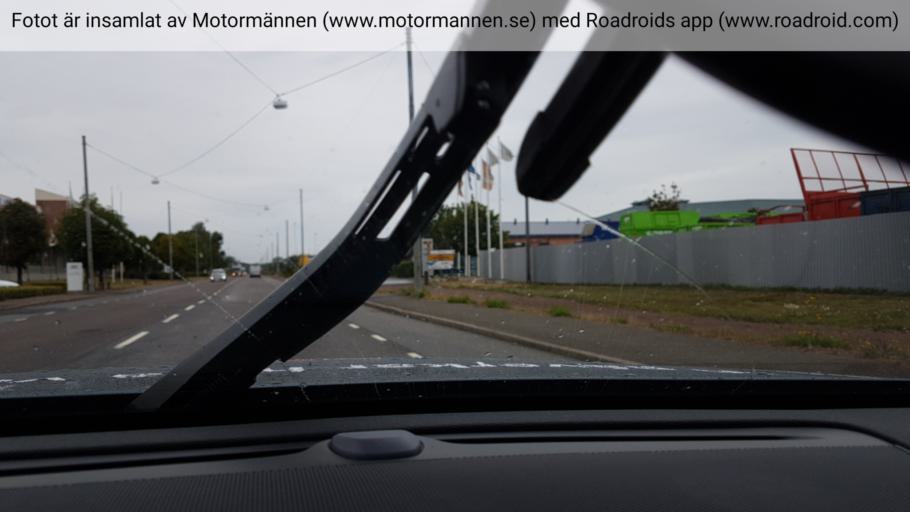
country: SE
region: Vaestra Goetaland
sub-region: Goteborg
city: Hammarkullen
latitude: 57.7501
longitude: 11.9962
